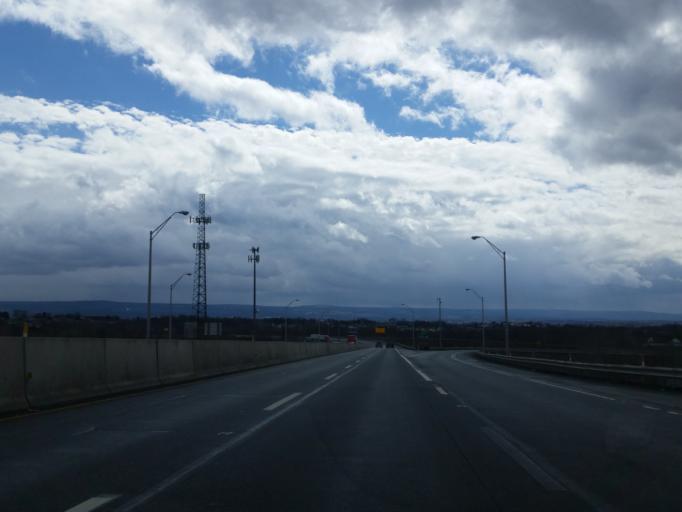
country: US
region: Pennsylvania
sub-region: Lackawanna County
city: Old Forge
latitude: 41.3930
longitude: -75.7321
